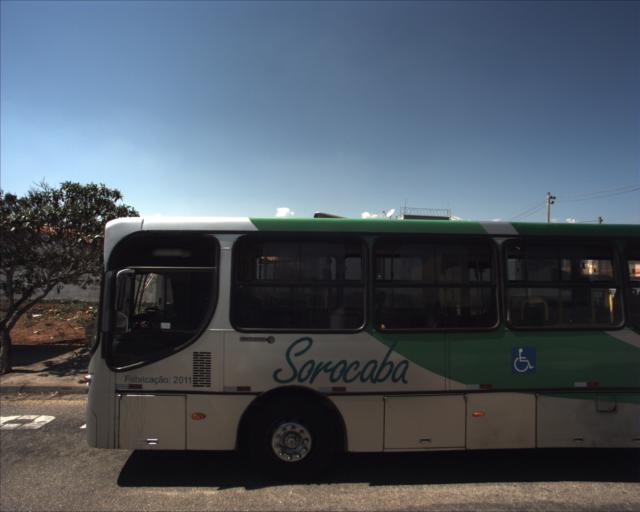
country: BR
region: Sao Paulo
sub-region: Sorocaba
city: Sorocaba
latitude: -23.5101
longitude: -47.5133
